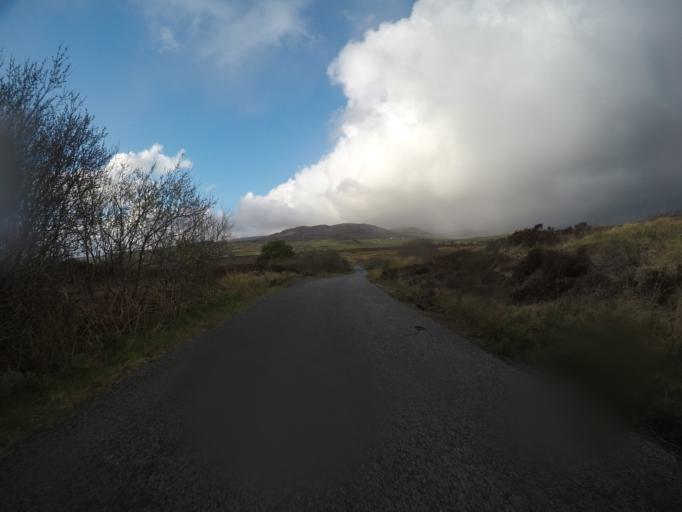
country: GB
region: Scotland
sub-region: Highland
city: Portree
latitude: 57.4710
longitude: -6.2992
